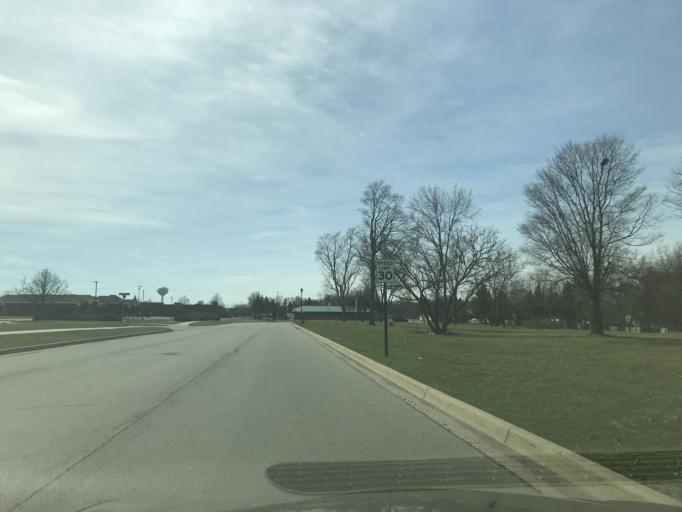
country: US
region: Michigan
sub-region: Eaton County
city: Grand Ledge
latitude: 42.7418
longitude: -84.7356
